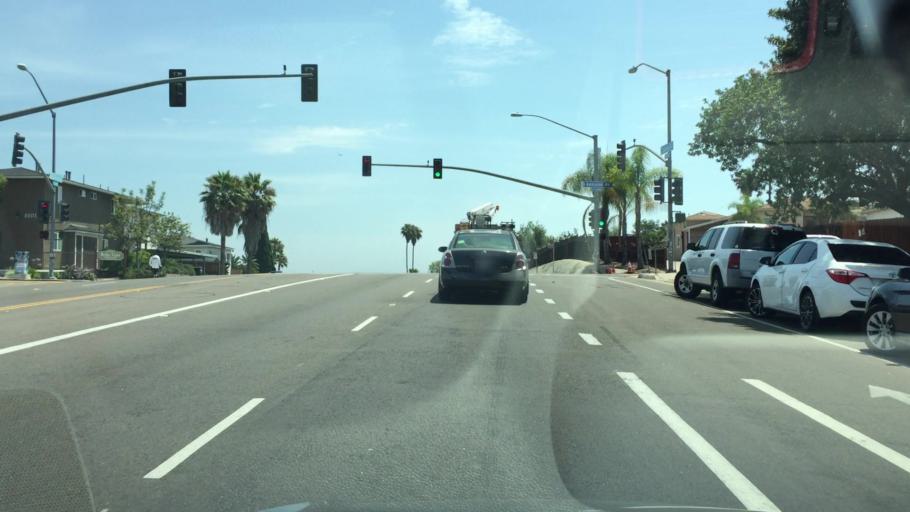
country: US
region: California
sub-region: San Diego County
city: Lemon Grove
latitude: 32.7581
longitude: -117.0664
